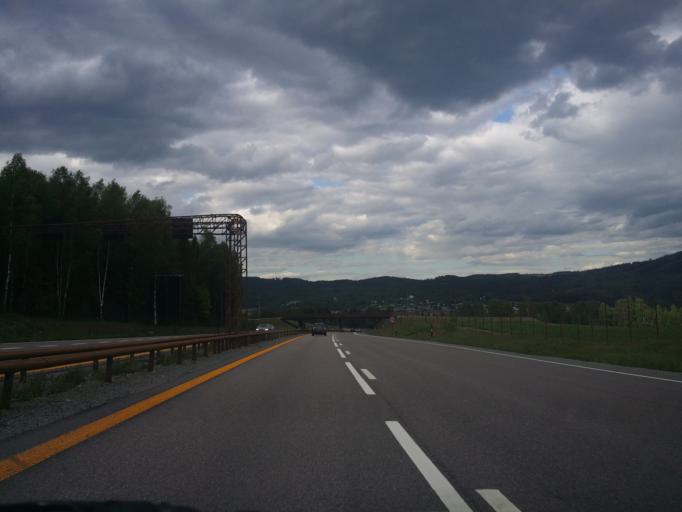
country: NO
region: Akershus
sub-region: Eidsvoll
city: Eidsvoll
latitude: 60.3915
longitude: 11.2185
